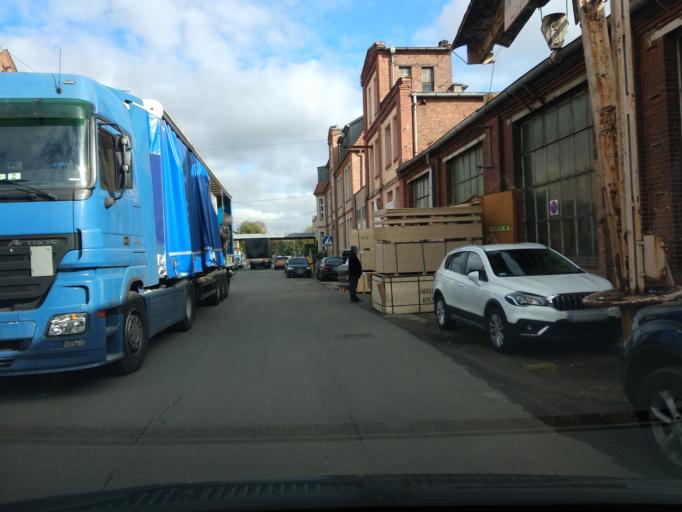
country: PL
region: Lower Silesian Voivodeship
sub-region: Powiat wroclawski
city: Wroclaw
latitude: 51.1111
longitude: 16.9886
